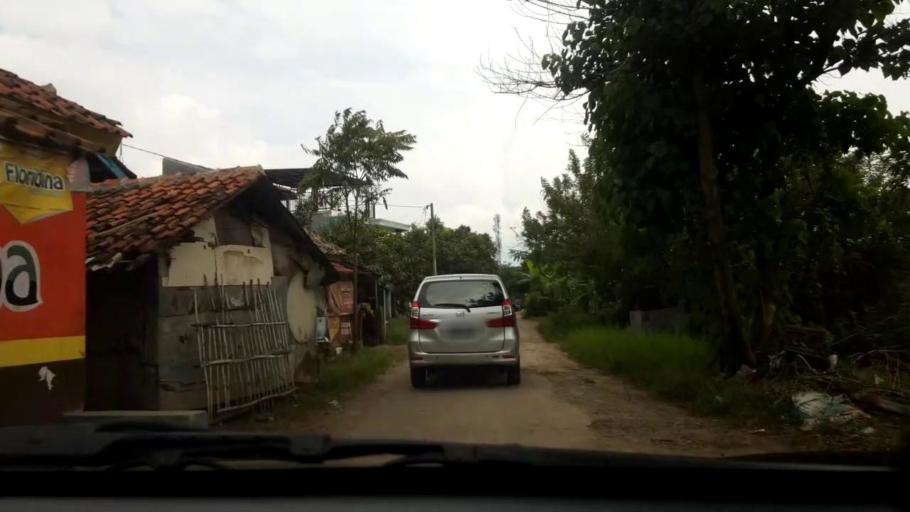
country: ID
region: West Java
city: Cileunyi
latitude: -6.9563
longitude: 107.7156
